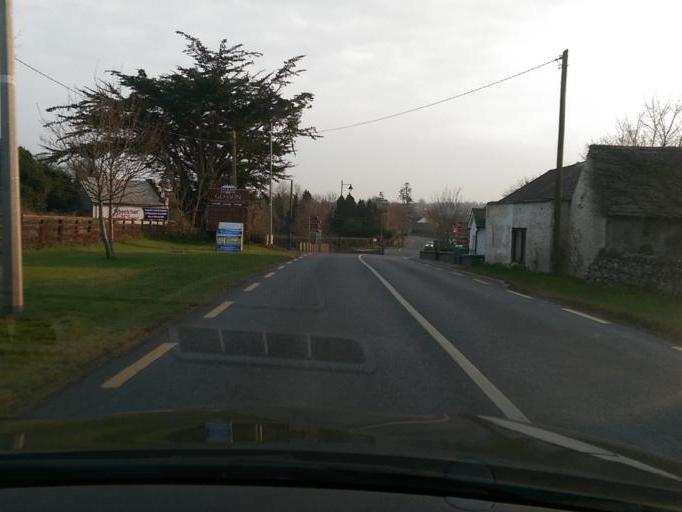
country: IE
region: Leinster
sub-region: An Iarmhi
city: Athlone
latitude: 53.4749
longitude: -7.8626
